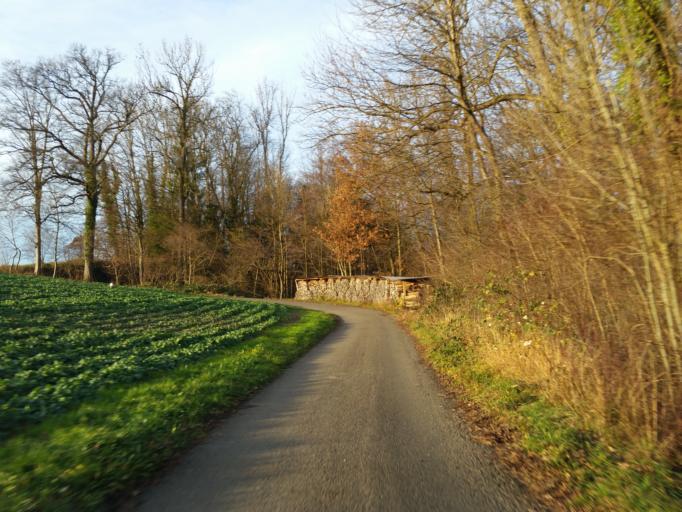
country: CH
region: Thurgau
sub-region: Arbon District
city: Amriswil
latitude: 47.5573
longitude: 9.3209
